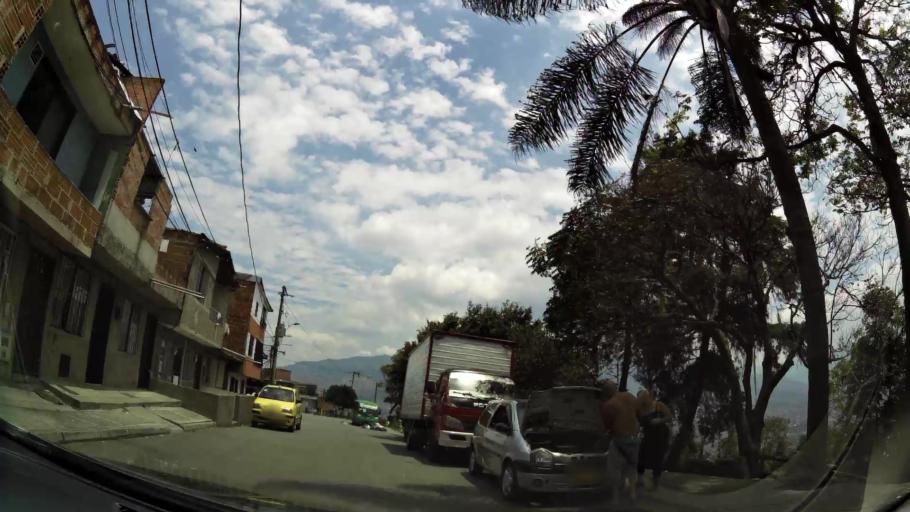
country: CO
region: Antioquia
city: Medellin
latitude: 6.2941
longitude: -75.5847
